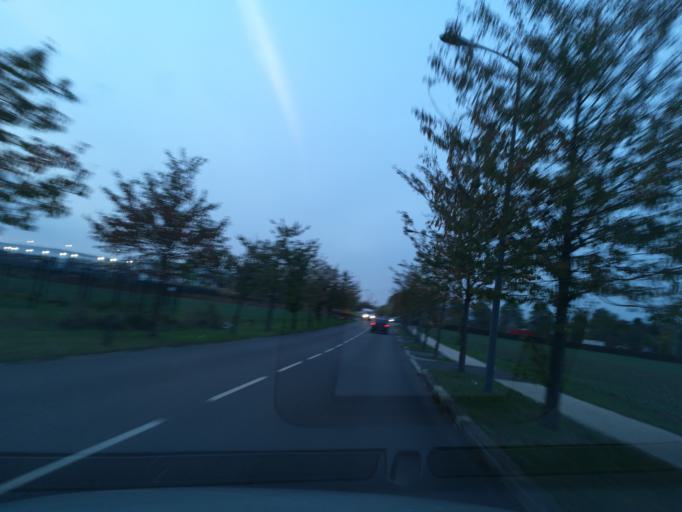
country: FR
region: Haute-Normandie
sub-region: Departement de la Seine-Maritime
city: Isneauville
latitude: 49.4872
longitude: 1.1465
